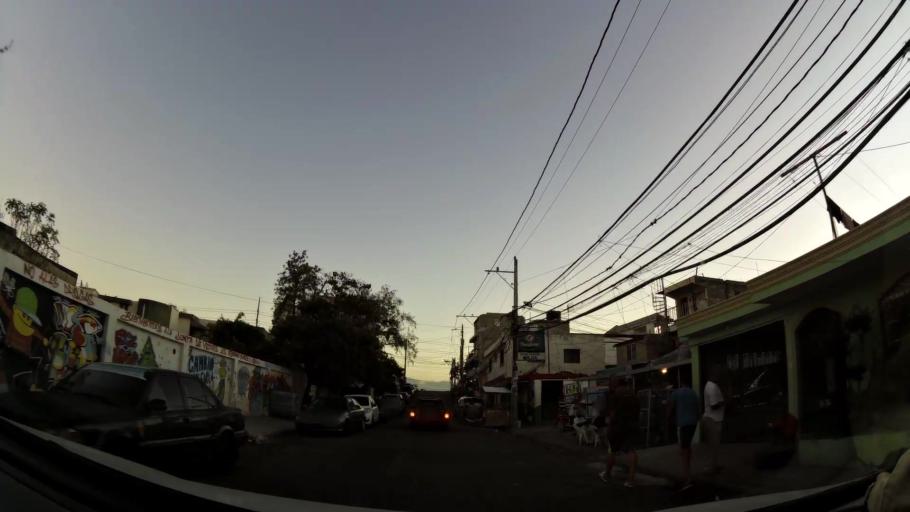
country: DO
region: Nacional
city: La Agustina
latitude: 18.5021
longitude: -69.9520
